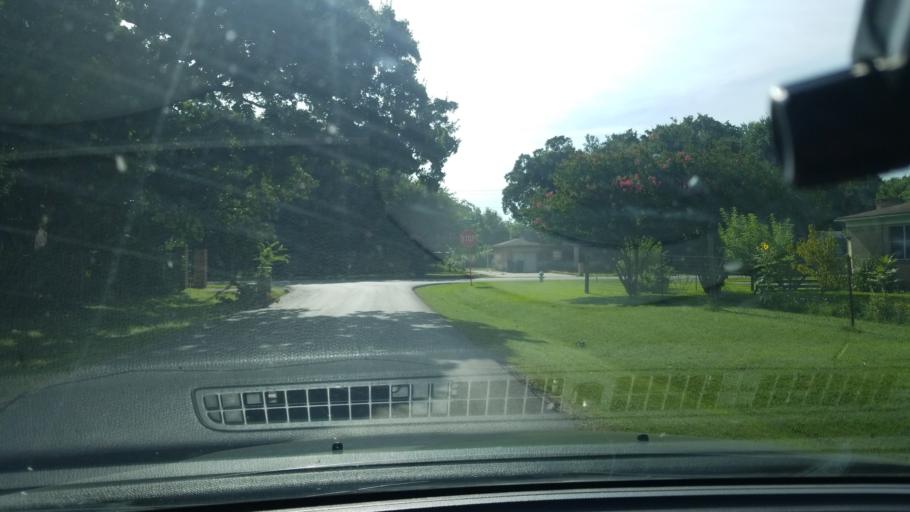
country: US
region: Texas
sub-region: Dallas County
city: Balch Springs
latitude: 32.7149
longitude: -96.6408
